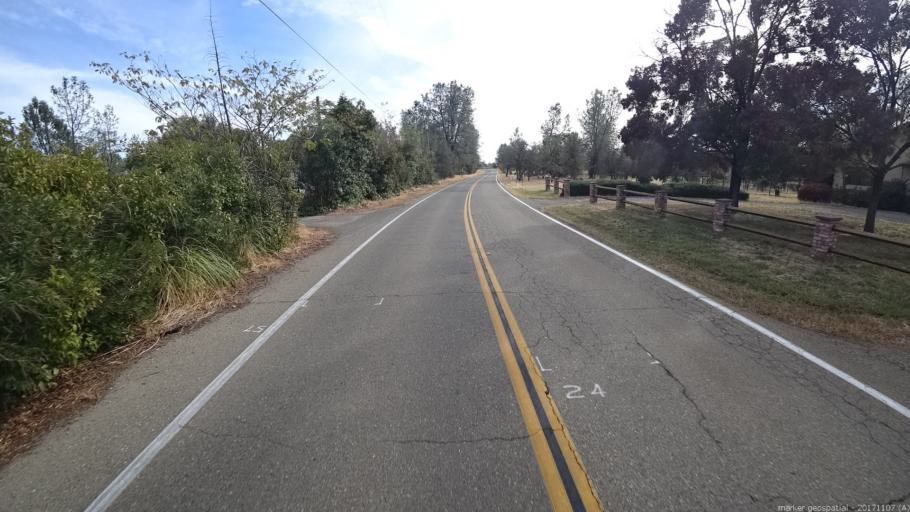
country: US
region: California
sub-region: Shasta County
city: Shasta
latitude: 40.4801
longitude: -122.4961
